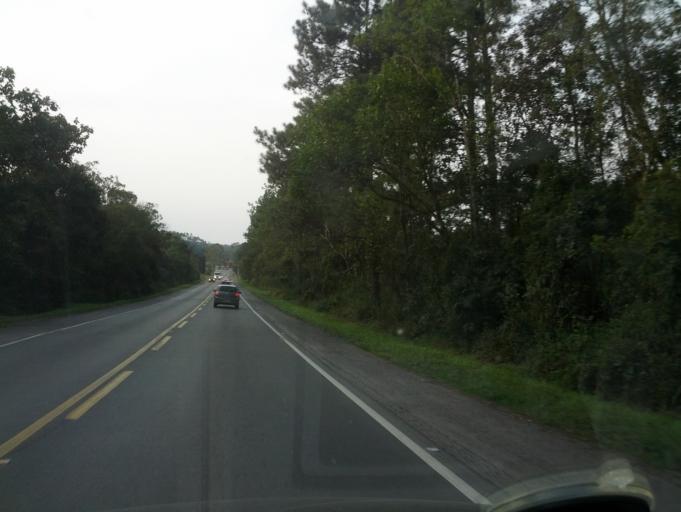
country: BR
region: Santa Catarina
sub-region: Otacilio Costa
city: Otacilio Costa
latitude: -27.2906
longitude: -50.0778
